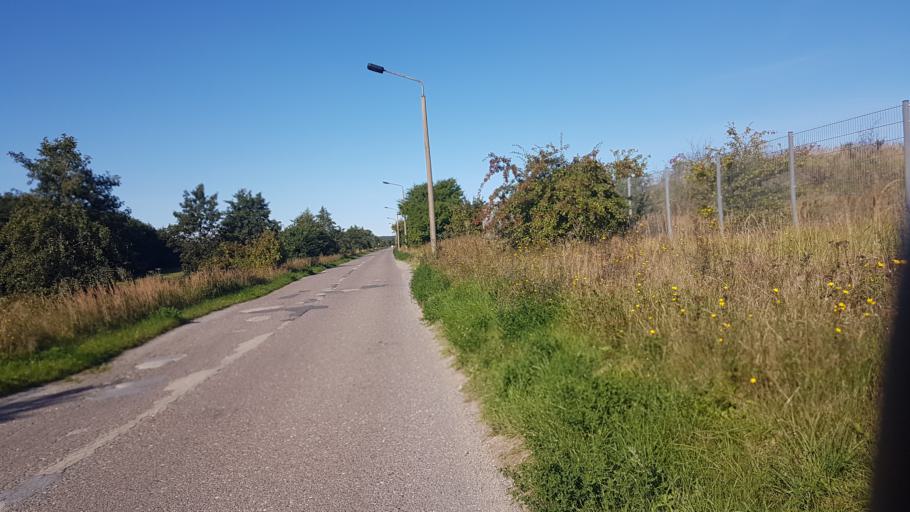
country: DE
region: Mecklenburg-Vorpommern
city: Sagard
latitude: 54.4922
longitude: 13.5675
